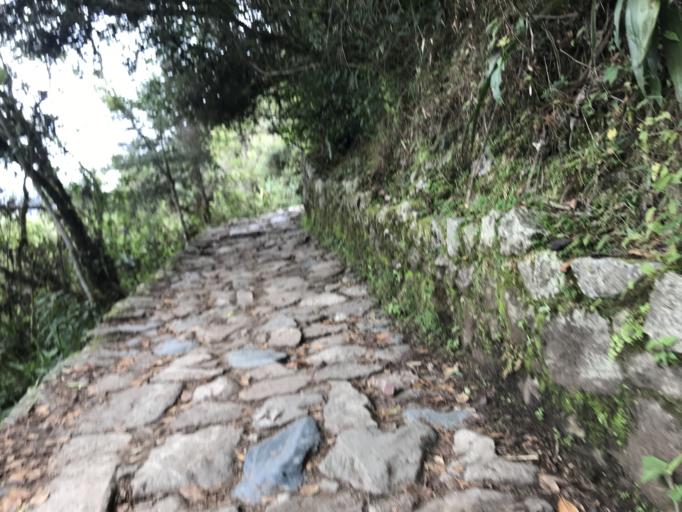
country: PE
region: Cusco
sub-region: Provincia de La Convencion
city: Santa Teresa
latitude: -13.1705
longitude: -72.5373
